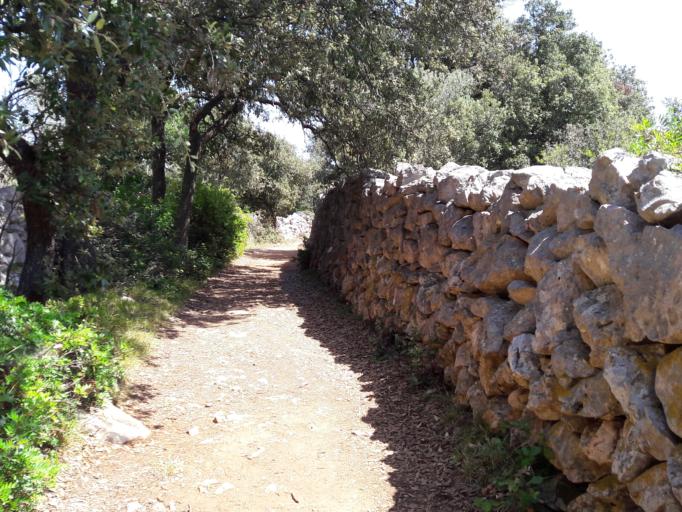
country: HR
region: Licko-Senjska
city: Novalja
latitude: 44.3640
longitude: 14.7007
